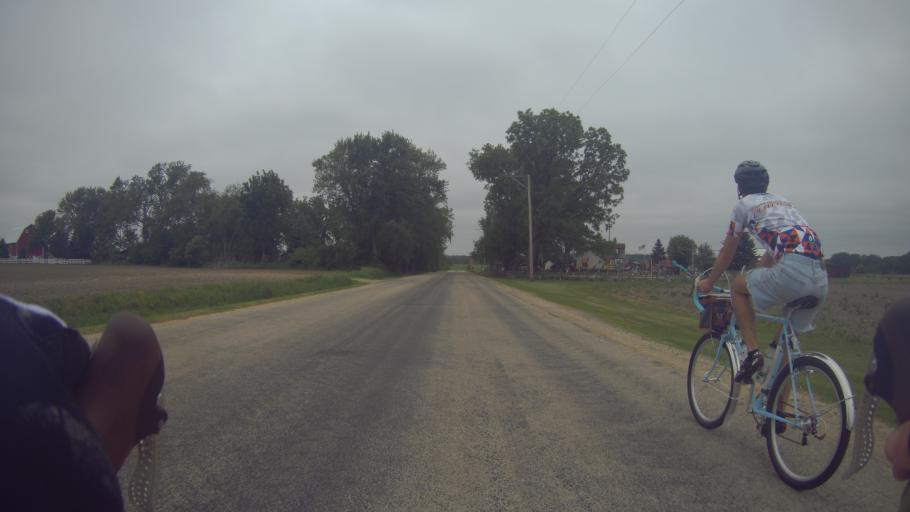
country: US
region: Wisconsin
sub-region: Green County
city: Brooklyn
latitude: 42.8477
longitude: -89.4130
